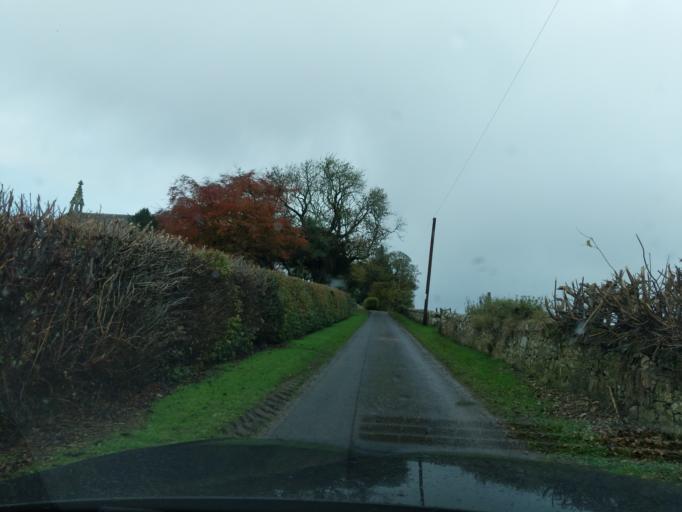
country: GB
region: Scotland
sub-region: Fife
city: Pittenweem
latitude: 56.2881
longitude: -2.7420
